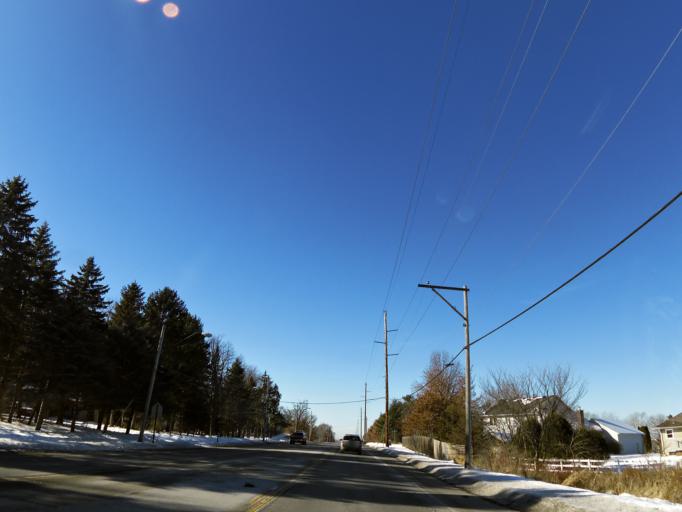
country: US
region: Minnesota
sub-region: Washington County
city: Oakdale
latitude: 44.9632
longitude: -92.9731
